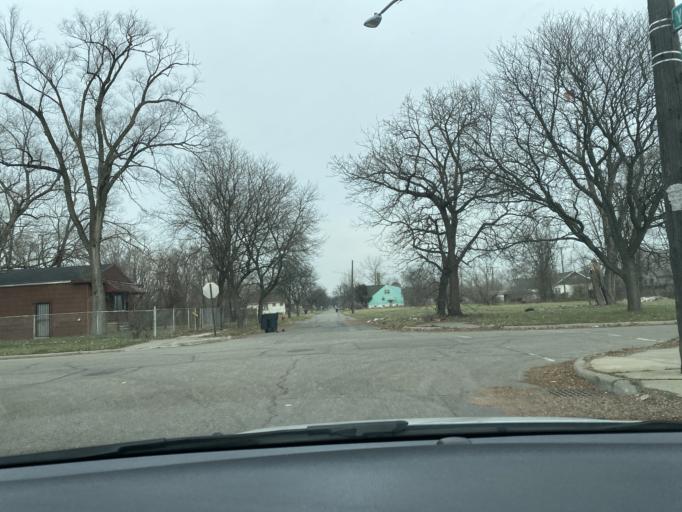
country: US
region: Michigan
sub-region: Wayne County
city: Highland Park
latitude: 42.3709
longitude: -83.1309
